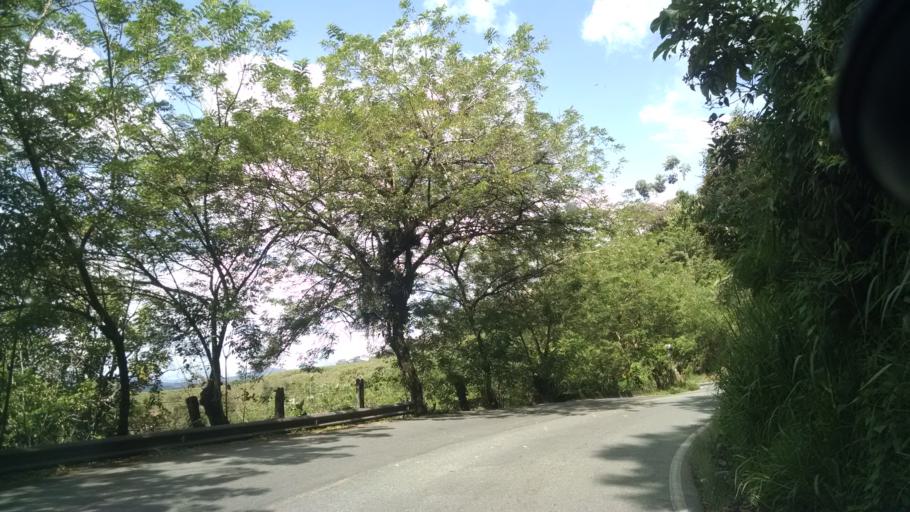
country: CO
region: Antioquia
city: Santo Domingo
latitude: 6.5324
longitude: -75.2350
